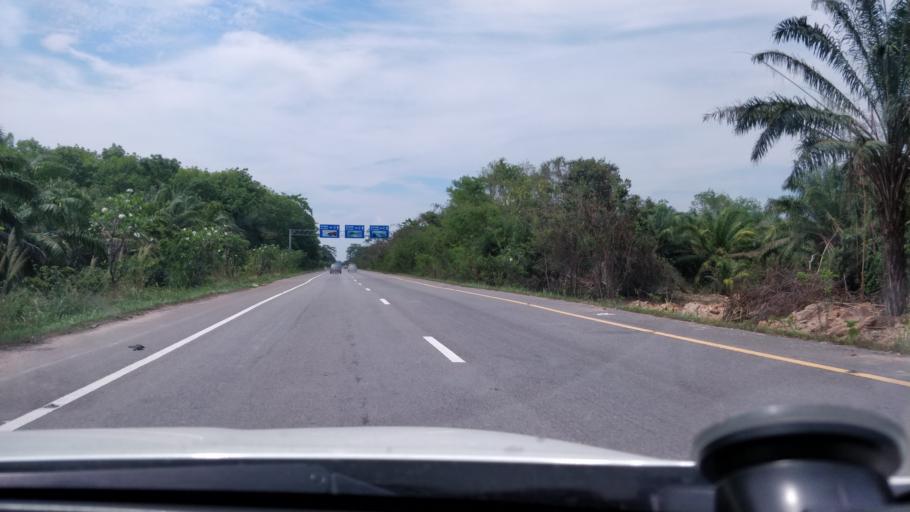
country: TH
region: Surat Thani
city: Khian Sa
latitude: 8.7640
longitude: 99.1611
